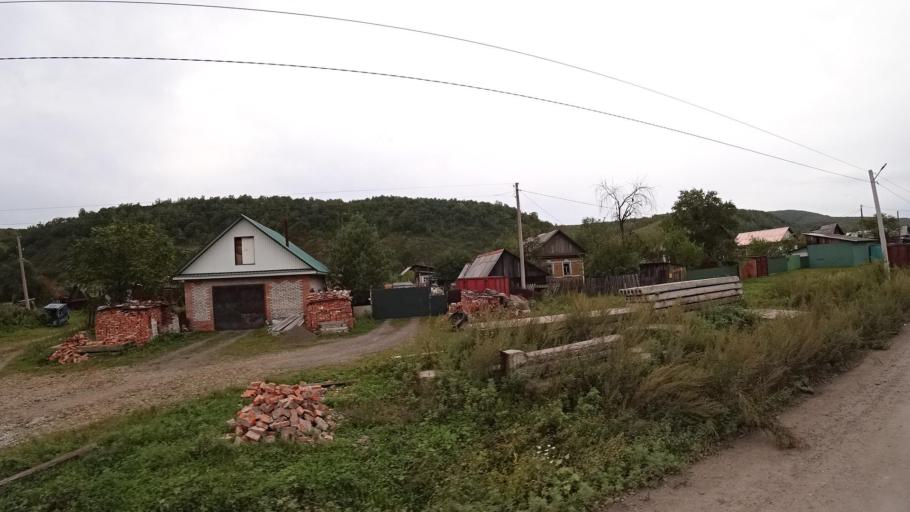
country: RU
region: Jewish Autonomous Oblast
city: Khingansk
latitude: 49.0209
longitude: 131.0484
